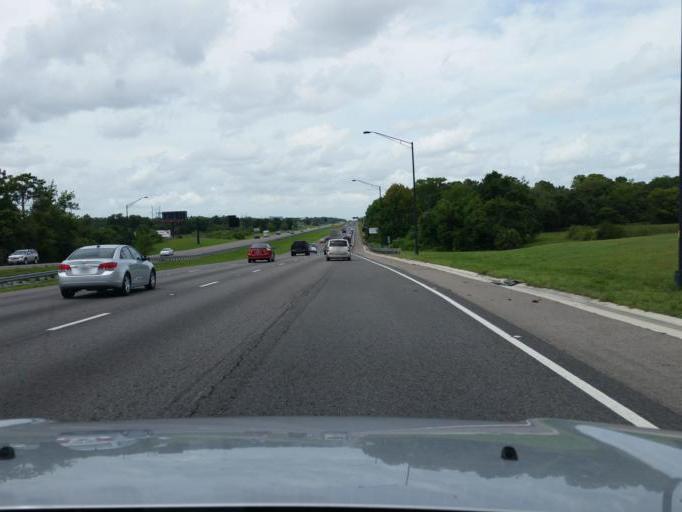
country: US
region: Florida
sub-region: Polk County
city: Loughman
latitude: 28.2761
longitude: -81.5991
